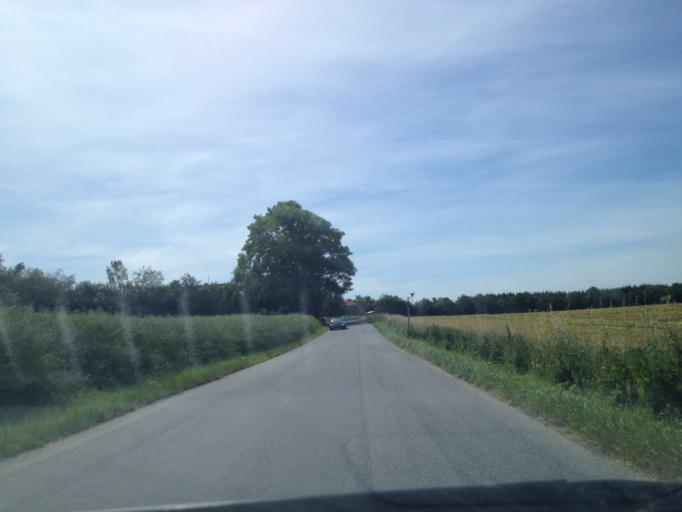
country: DK
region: Central Jutland
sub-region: Samso Kommune
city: Tranebjerg
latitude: 55.8422
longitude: 10.6177
